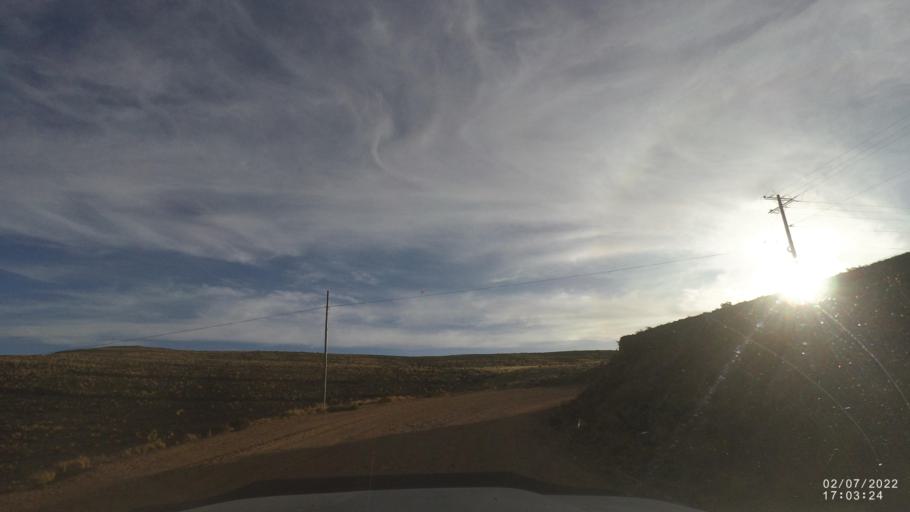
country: BO
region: Cochabamba
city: Irpa Irpa
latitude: -17.9233
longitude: -66.5560
